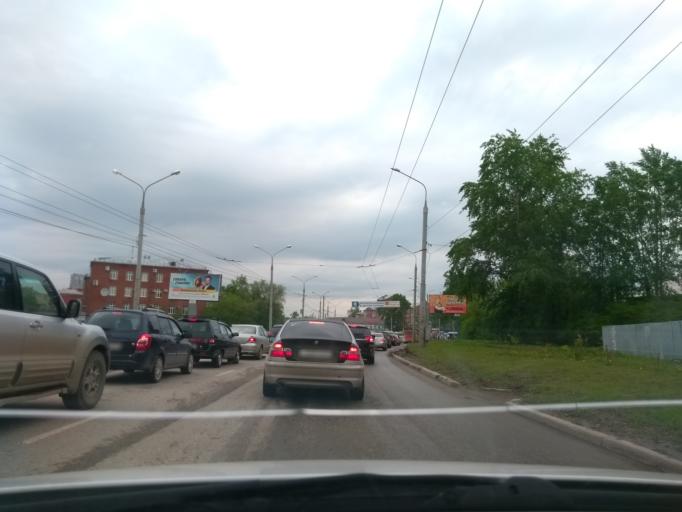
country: RU
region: Perm
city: Perm
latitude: 57.9834
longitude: 56.2469
